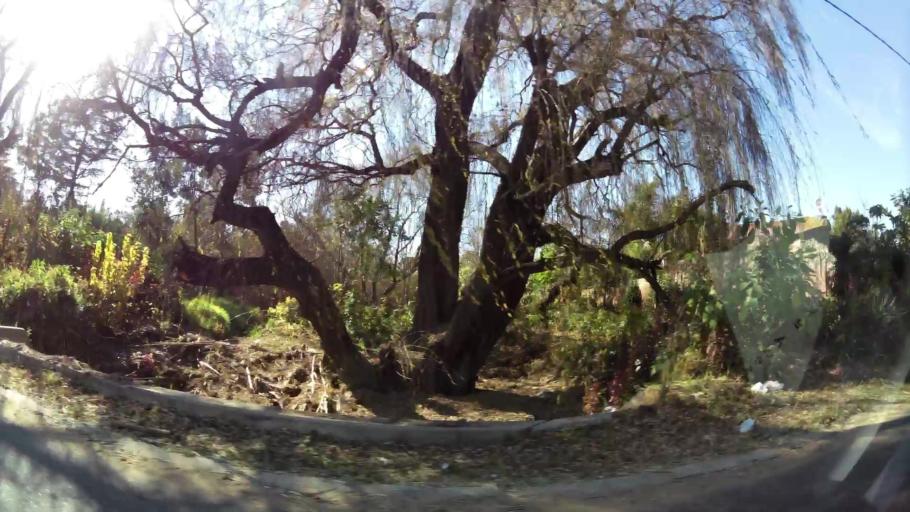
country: ZA
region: Gauteng
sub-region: City of Johannesburg Metropolitan Municipality
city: Modderfontein
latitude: -26.1156
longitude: 28.1152
